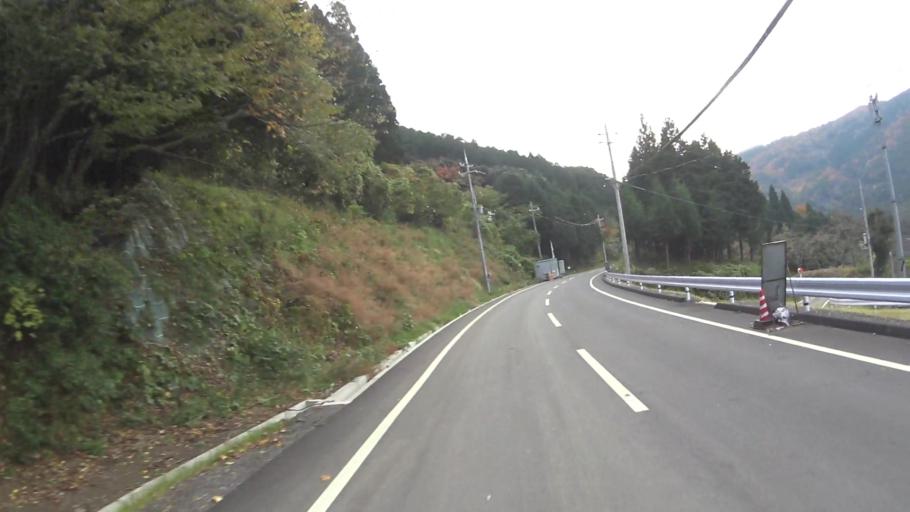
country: JP
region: Kyoto
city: Maizuru
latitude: 35.5667
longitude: 135.4593
